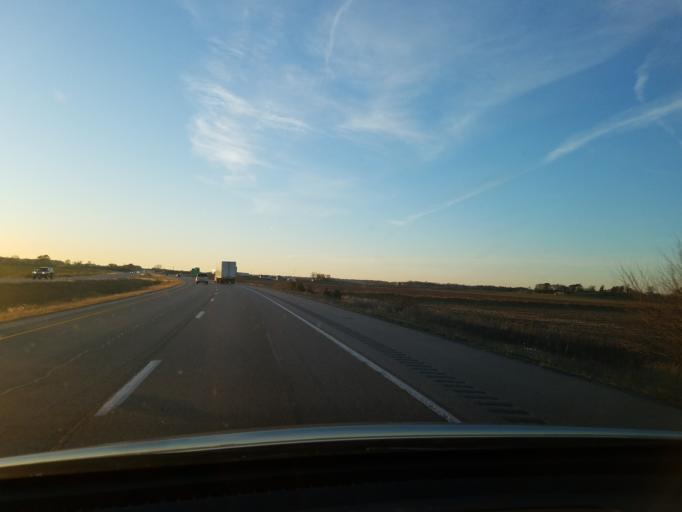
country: US
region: Indiana
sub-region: Posey County
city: Poseyville
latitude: 38.1838
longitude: -87.7698
